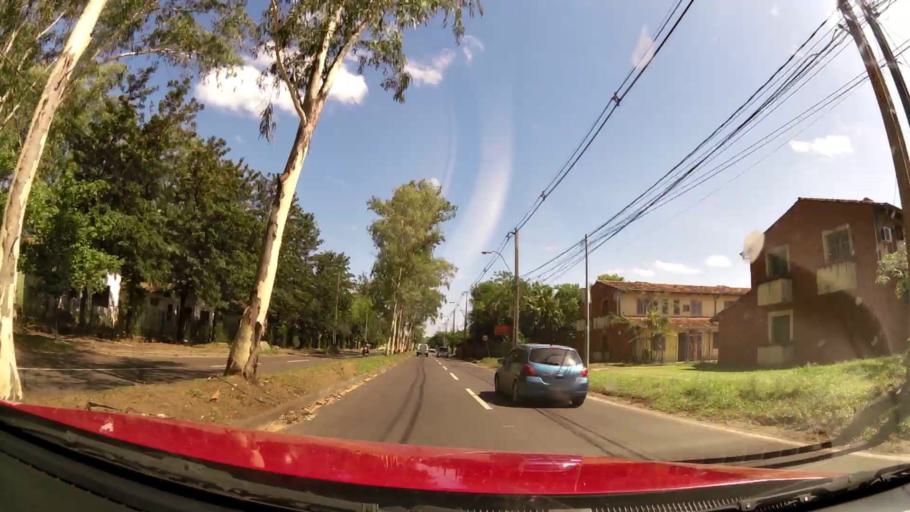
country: PY
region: Central
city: Colonia Mariano Roque Alonso
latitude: -25.2503
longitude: -57.5505
